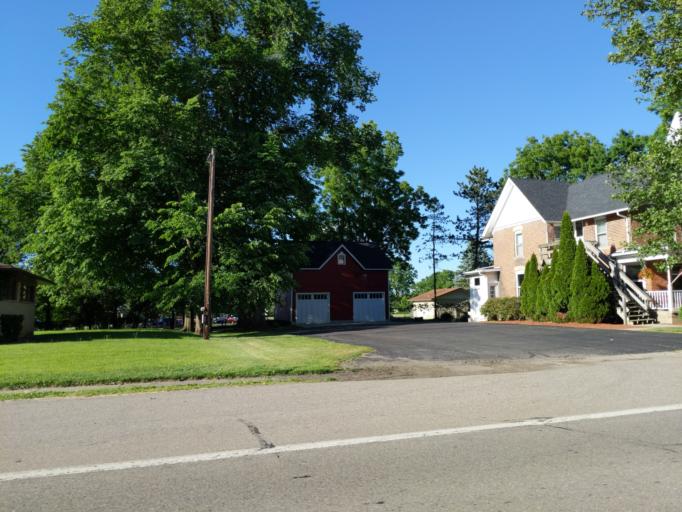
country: US
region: Michigan
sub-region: Ingham County
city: Stockbridge
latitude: 42.4520
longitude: -84.1828
